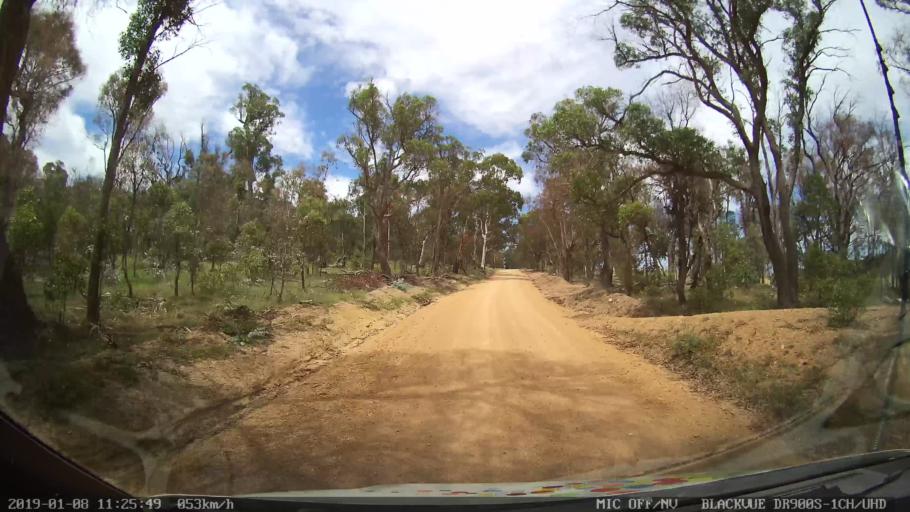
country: AU
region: New South Wales
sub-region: Guyra
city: Guyra
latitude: -30.2762
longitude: 151.5605
